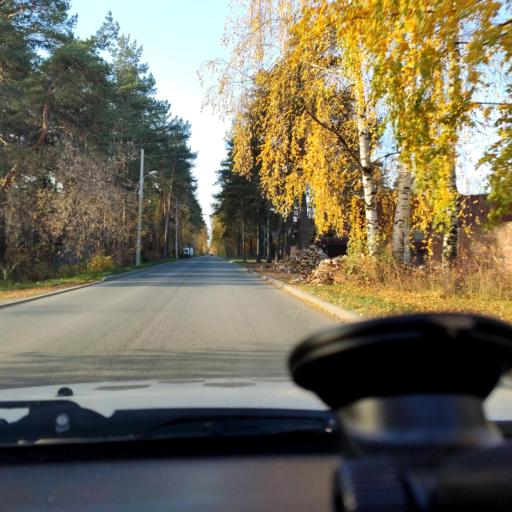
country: RU
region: Perm
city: Perm
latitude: 58.0525
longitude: 56.2936
